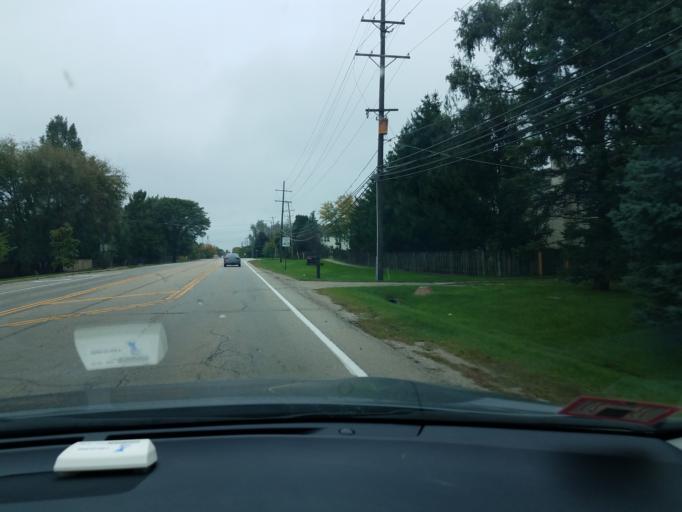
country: US
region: Illinois
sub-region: Lake County
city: Vernon Hills
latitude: 42.1915
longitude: -87.9554
